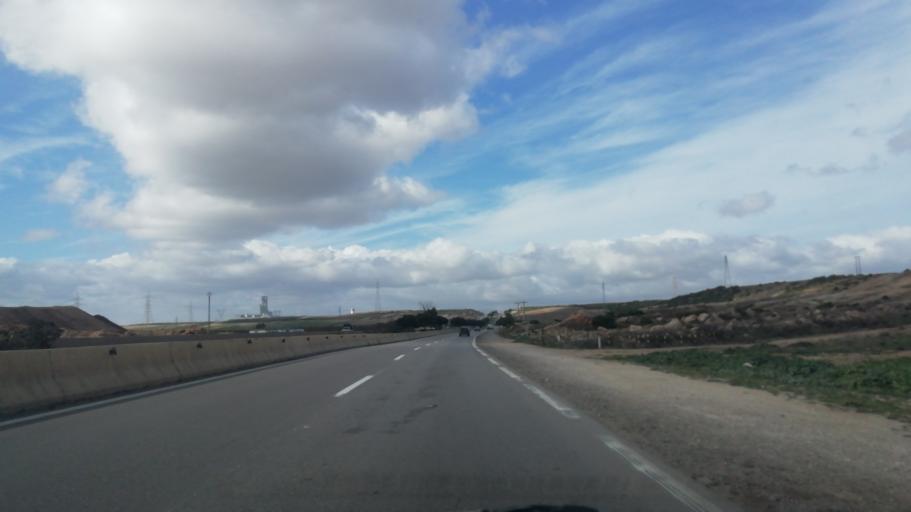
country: DZ
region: Oran
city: Ain el Bya
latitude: 35.7683
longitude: -0.2324
